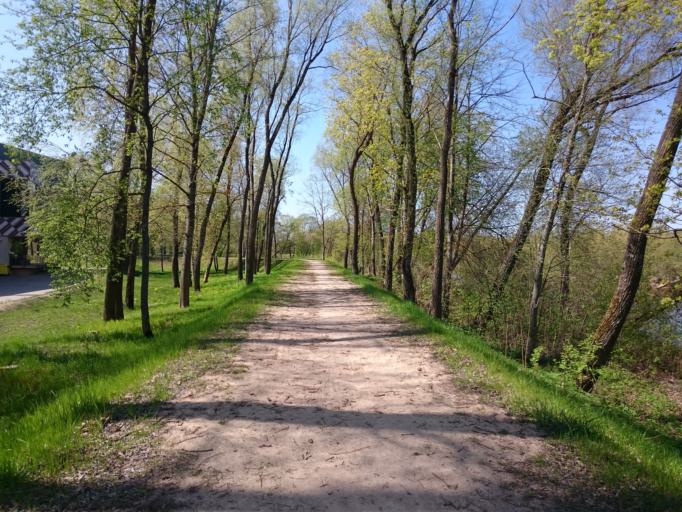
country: LV
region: Adazi
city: Adazi
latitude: 57.0806
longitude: 24.3330
